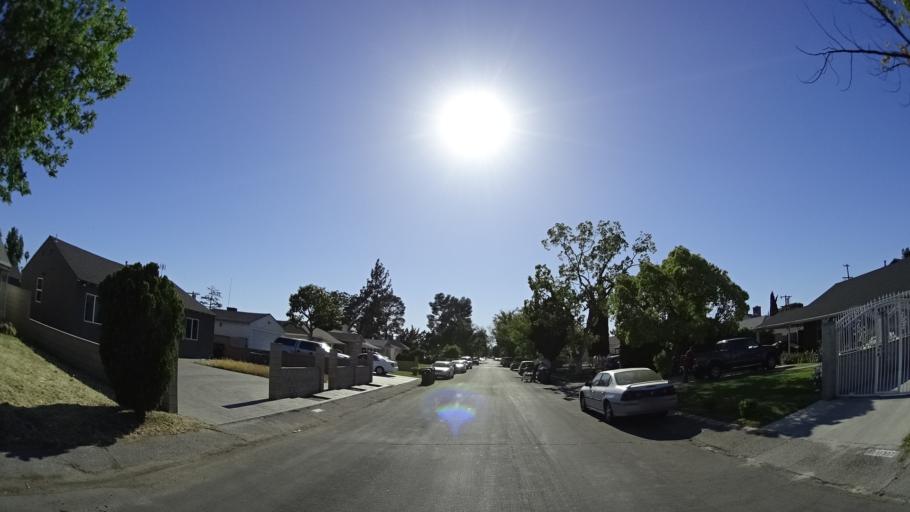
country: US
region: California
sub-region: Los Angeles County
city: North Hollywood
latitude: 34.1812
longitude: -118.3772
